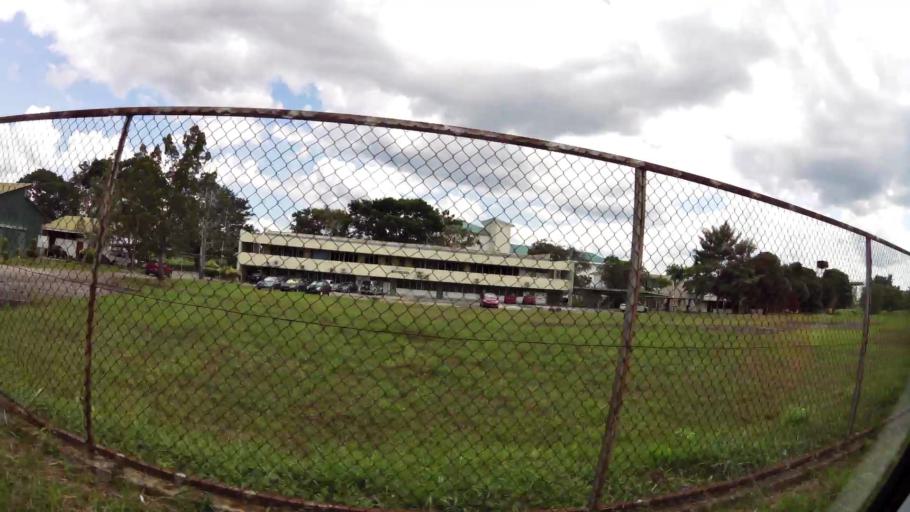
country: BN
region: Brunei and Muara
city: Bandar Seri Begawan
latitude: 4.9481
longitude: 114.9533
